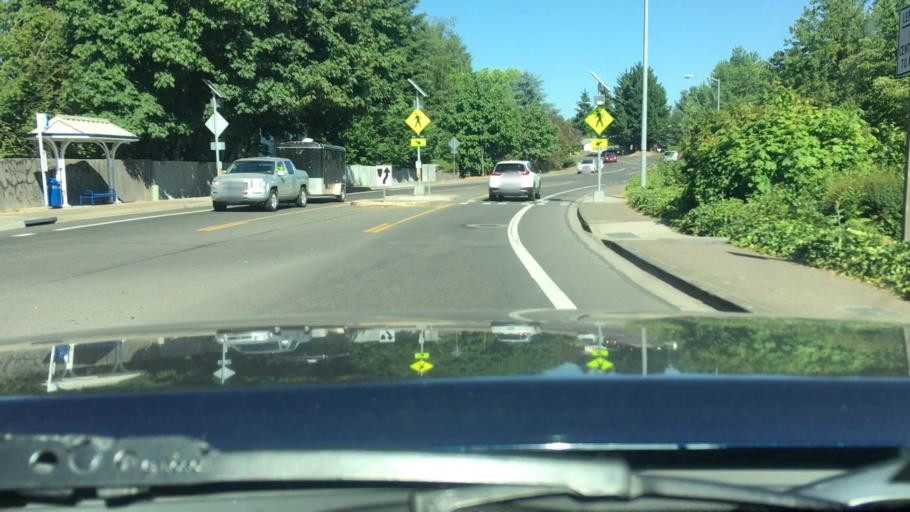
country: US
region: Oregon
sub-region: Lane County
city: Eugene
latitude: 44.0932
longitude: -123.0927
